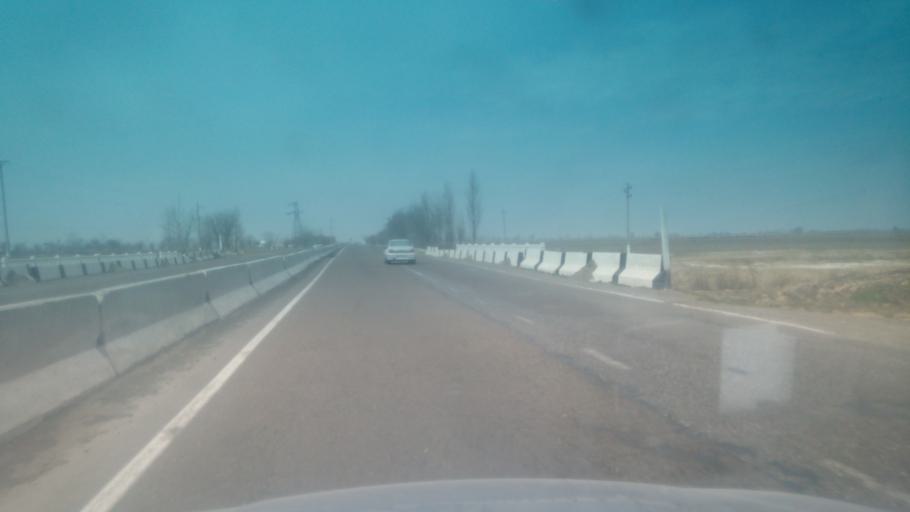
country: KZ
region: Ongtustik Qazaqstan
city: Myrzakent
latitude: 40.5227
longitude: 68.4583
